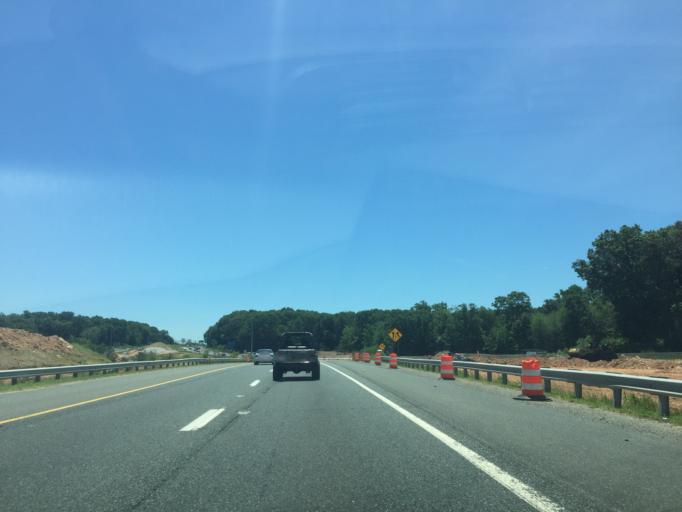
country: US
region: Maryland
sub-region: Baltimore County
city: Rossville
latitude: 39.3478
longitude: -76.4949
